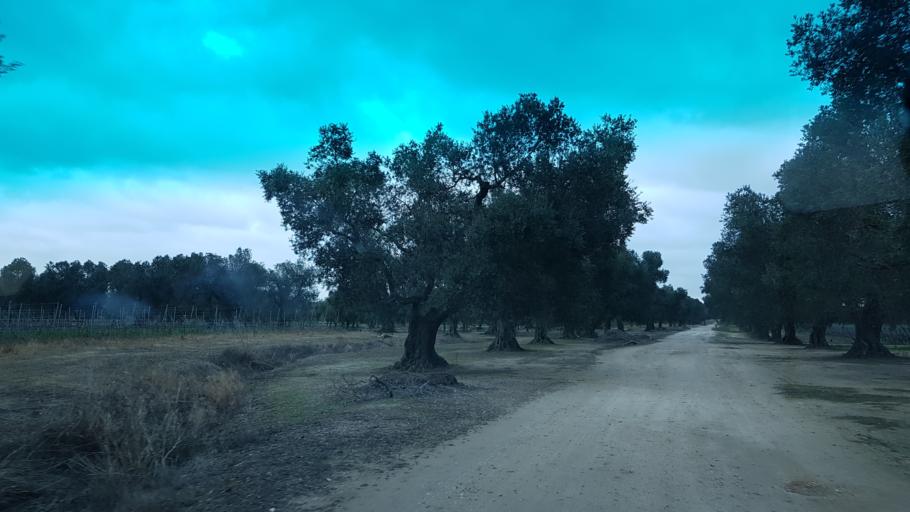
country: IT
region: Apulia
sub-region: Provincia di Brindisi
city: La Rosa
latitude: 40.5895
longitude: 17.9829
